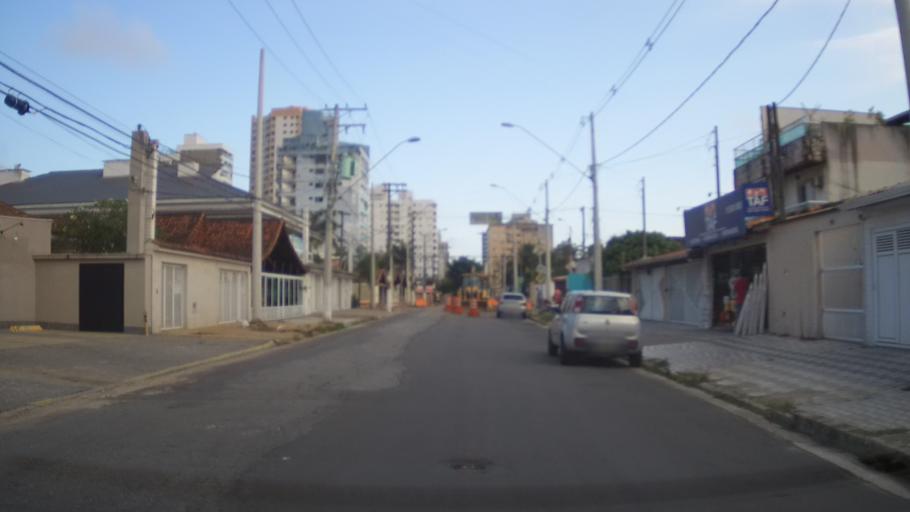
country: BR
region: Sao Paulo
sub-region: Praia Grande
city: Praia Grande
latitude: -24.0039
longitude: -46.4098
